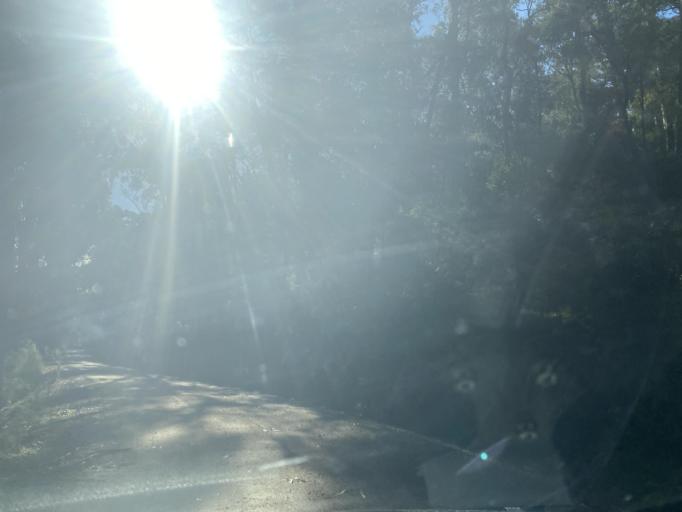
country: AU
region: Victoria
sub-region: Mansfield
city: Mansfield
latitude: -36.8325
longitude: 146.1682
